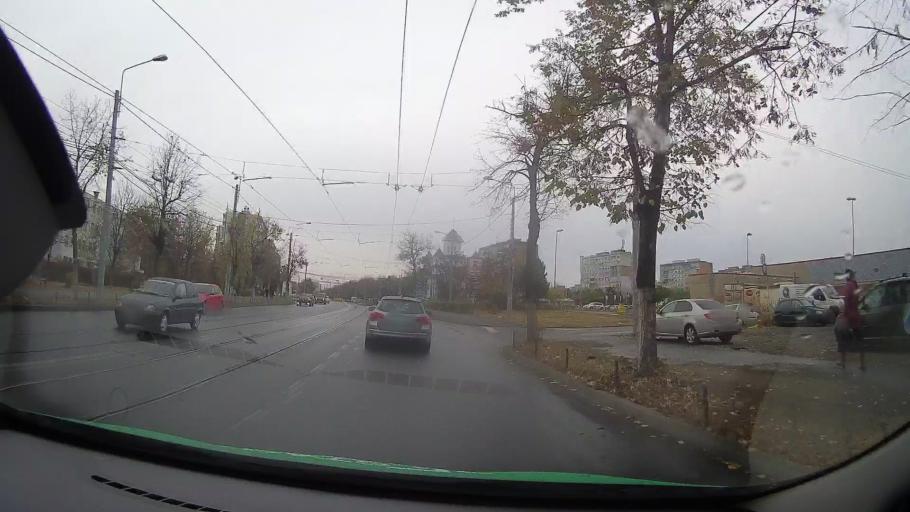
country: RO
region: Prahova
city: Ploiesti
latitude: 44.9396
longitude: 25.9904
